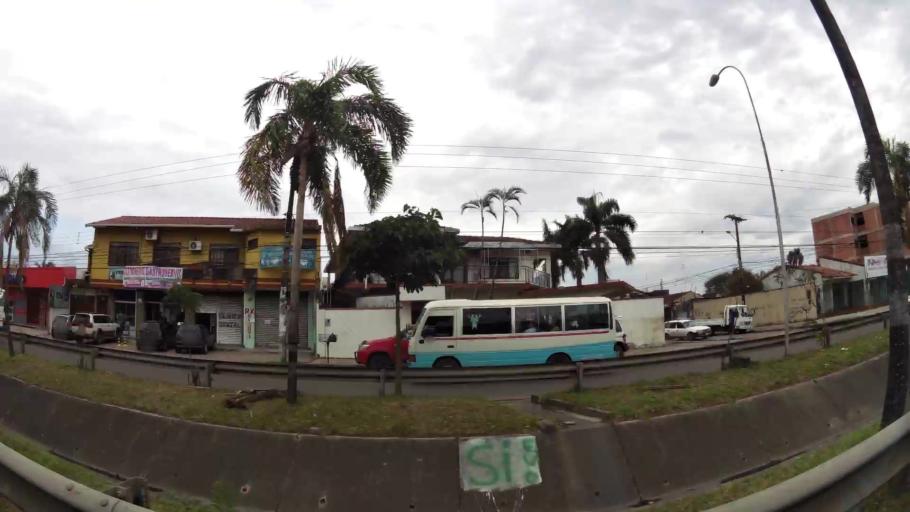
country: BO
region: Santa Cruz
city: Santa Cruz de la Sierra
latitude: -17.7699
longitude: -63.1662
